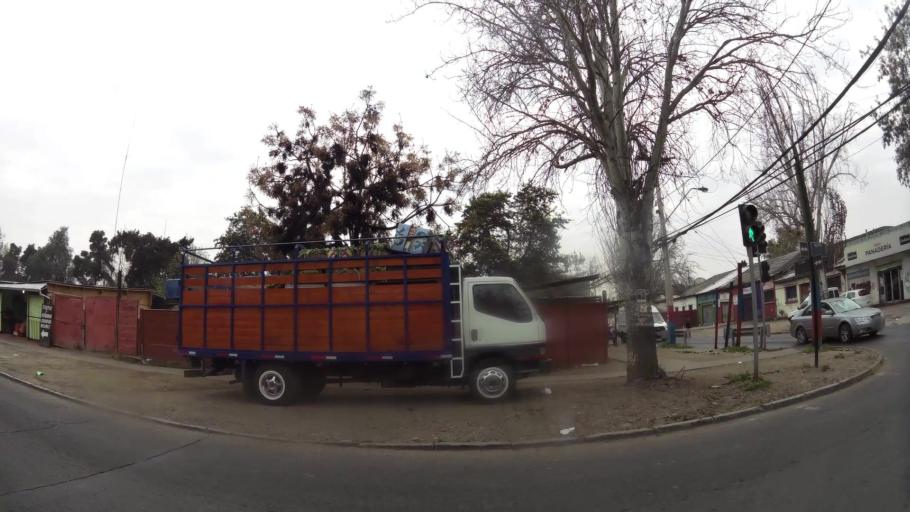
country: CL
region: Santiago Metropolitan
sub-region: Provincia de Santiago
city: Villa Presidente Frei, Nunoa, Santiago, Chile
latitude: -33.4863
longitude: -70.5899
